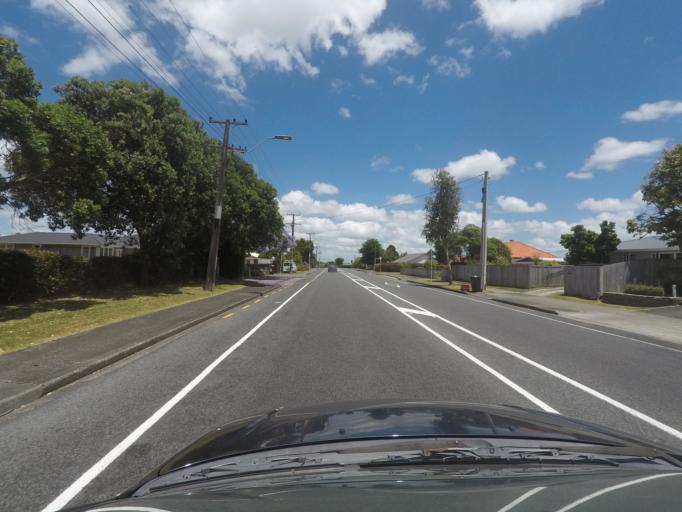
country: NZ
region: Northland
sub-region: Whangarei
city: Whangarei
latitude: -35.7583
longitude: 174.3677
